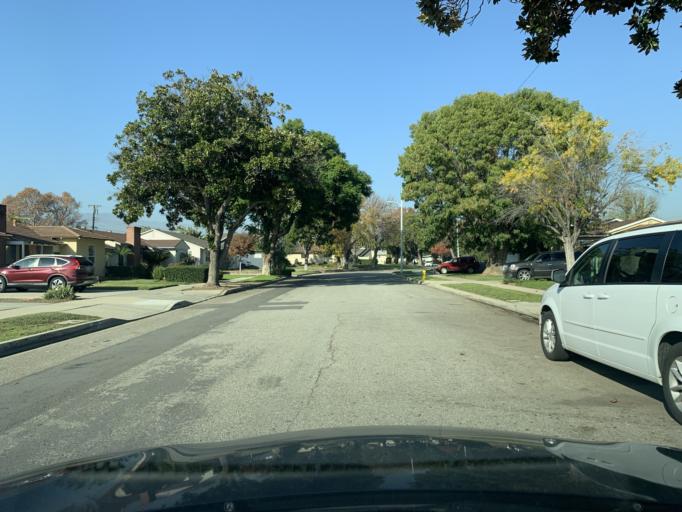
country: US
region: California
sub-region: Los Angeles County
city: Covina
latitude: 34.0803
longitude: -117.8953
